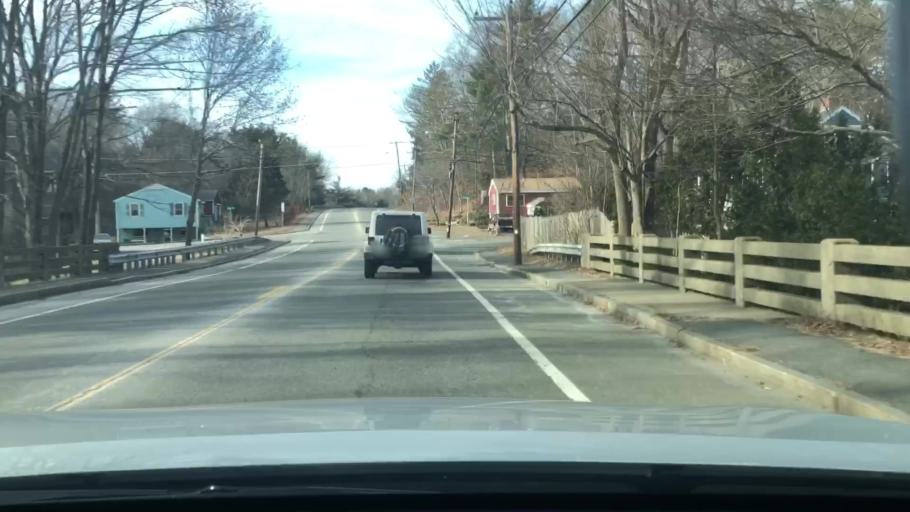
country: US
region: Massachusetts
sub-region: Worcester County
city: Upton
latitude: 42.1725
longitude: -71.6278
